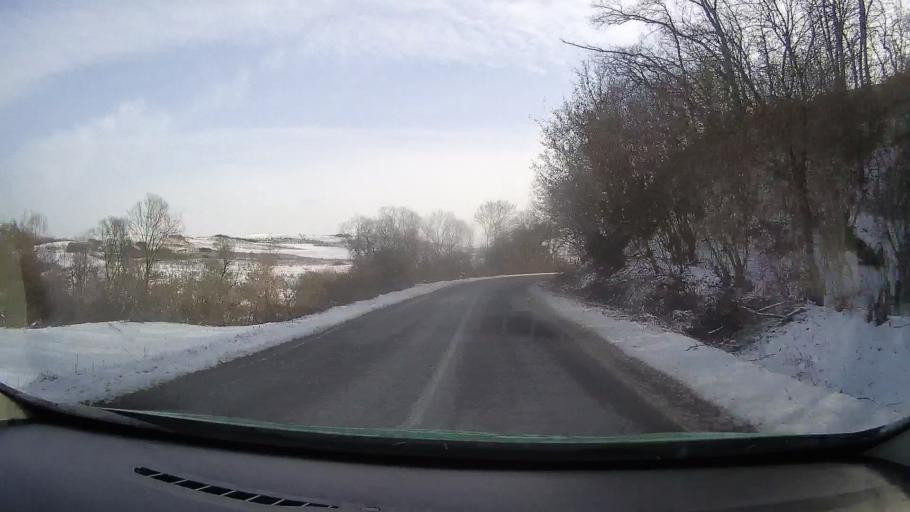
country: RO
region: Mures
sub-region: Comuna Apold
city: Saes
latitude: 46.1703
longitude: 24.7575
